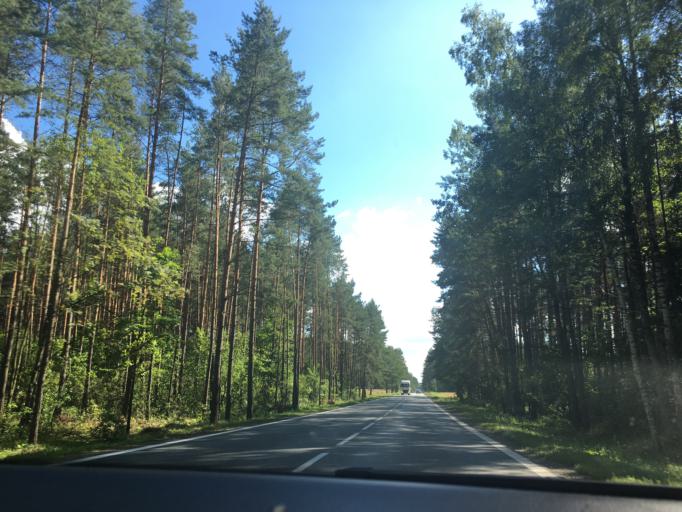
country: PL
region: Podlasie
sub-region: Powiat sokolski
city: Janow
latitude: 53.3650
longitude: 23.1064
